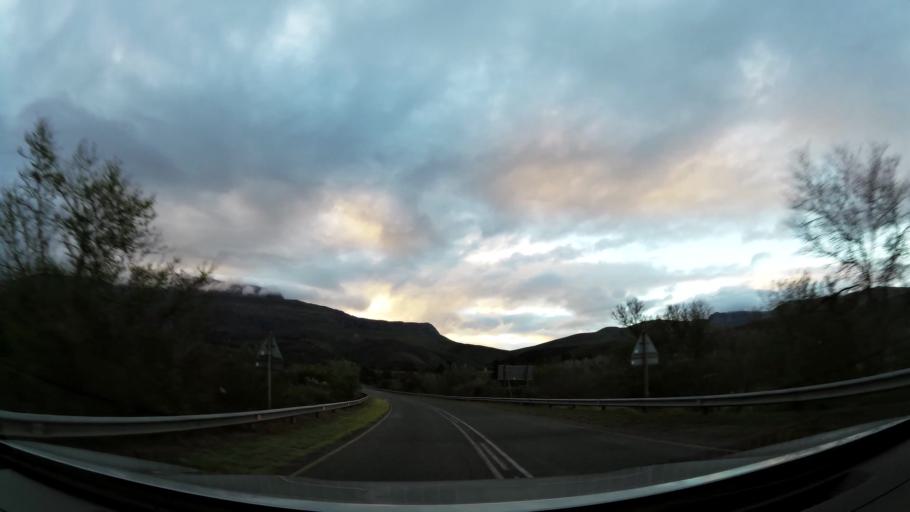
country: ZA
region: Western Cape
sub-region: Overberg District Municipality
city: Swellendam
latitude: -34.0069
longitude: 20.7080
